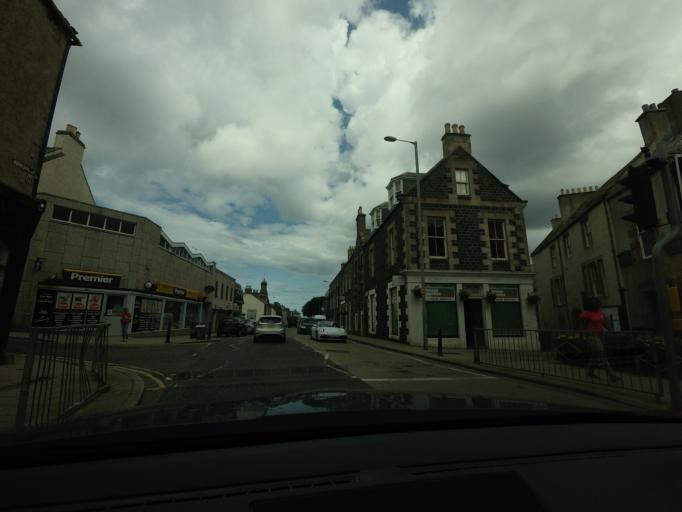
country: GB
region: Scotland
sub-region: Aberdeenshire
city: Banff
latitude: 57.6648
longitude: -2.5234
